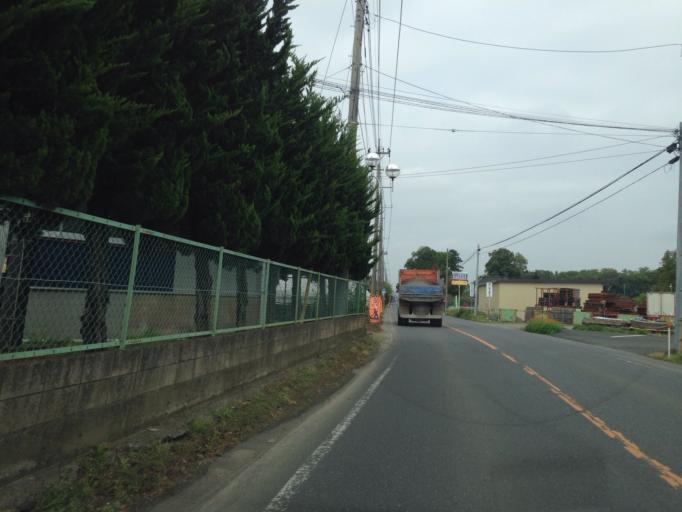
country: JP
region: Ibaraki
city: Ishige
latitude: 36.1679
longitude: 139.8859
